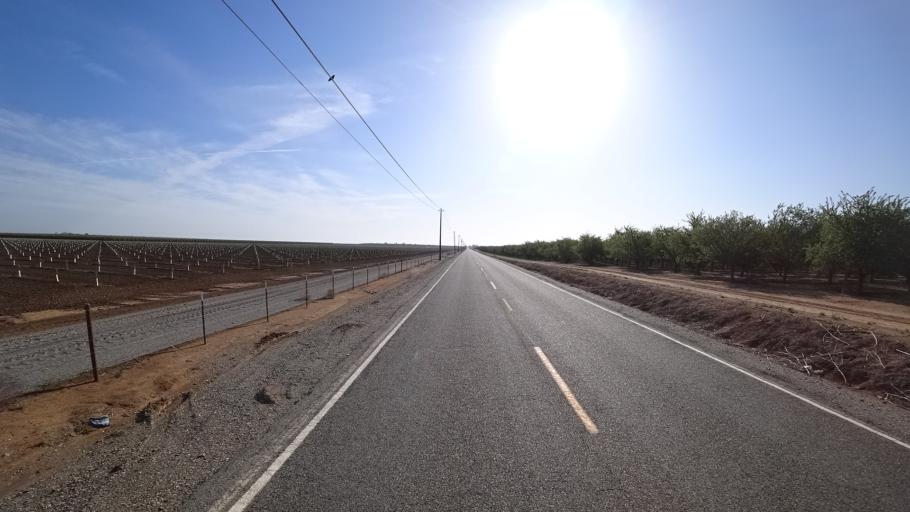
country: US
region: California
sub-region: Glenn County
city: Willows
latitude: 39.5389
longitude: -122.2440
